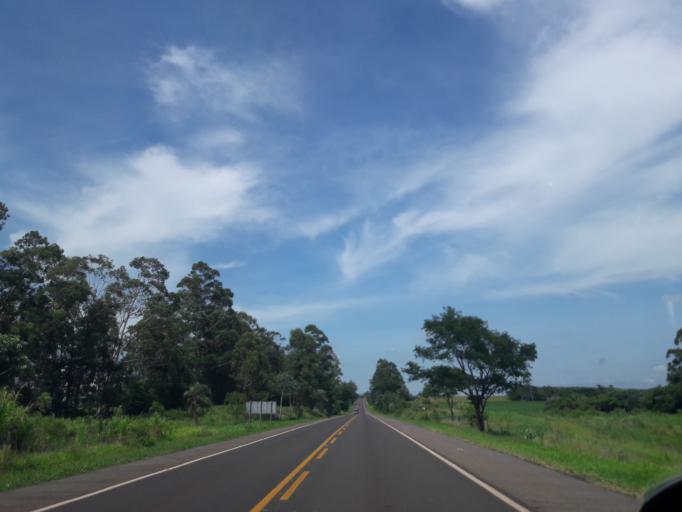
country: BR
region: Parana
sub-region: Campo Mourao
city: Campo Mourao
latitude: -24.2781
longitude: -52.5256
